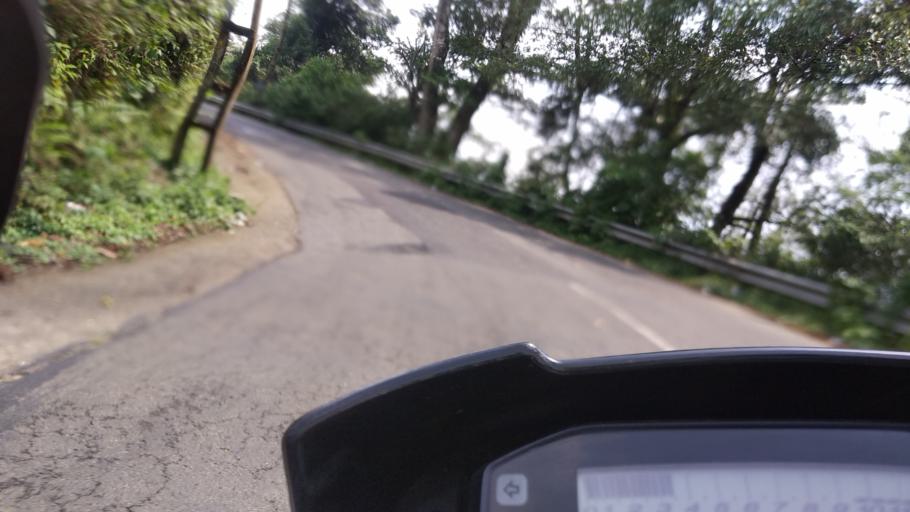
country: IN
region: Kerala
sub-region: Kottayam
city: Erattupetta
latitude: 9.6291
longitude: 76.9783
